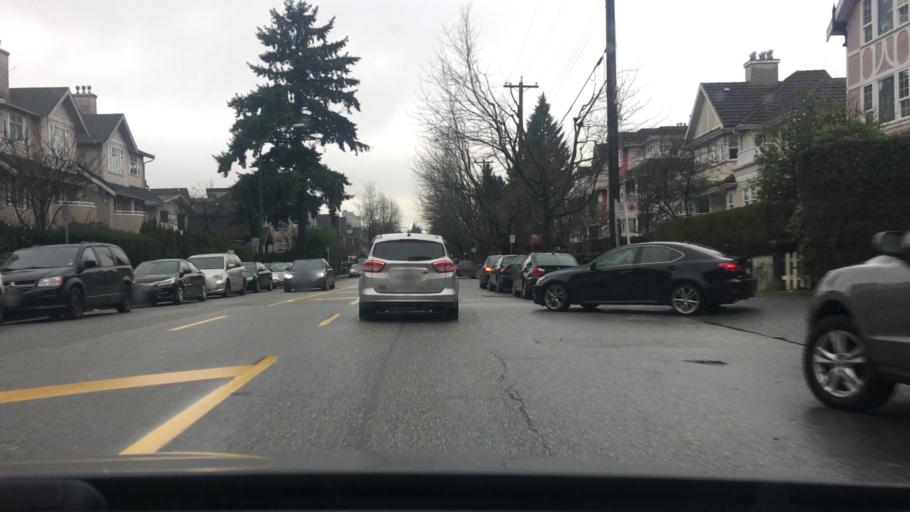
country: CA
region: British Columbia
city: Vancouver
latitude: 49.2570
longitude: -123.1161
